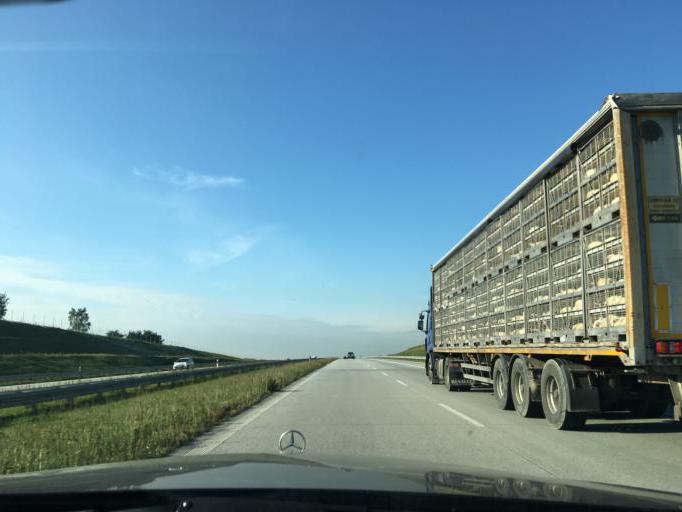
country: PL
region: Lodz Voivodeship
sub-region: Powiat lodzki wschodni
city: Andrespol
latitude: 51.8125
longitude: 19.6360
